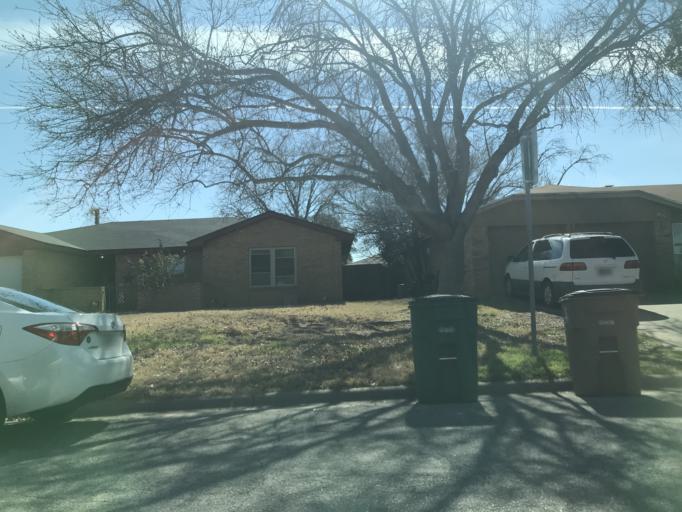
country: US
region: Texas
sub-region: Tom Green County
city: San Angelo
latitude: 31.4358
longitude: -100.4917
